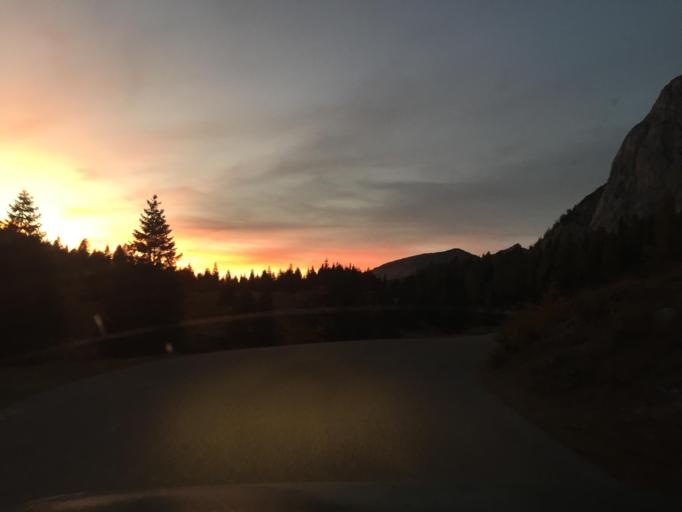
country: IT
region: Veneto
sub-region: Provincia di Belluno
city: Granvilla
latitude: 46.6216
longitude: 12.7128
